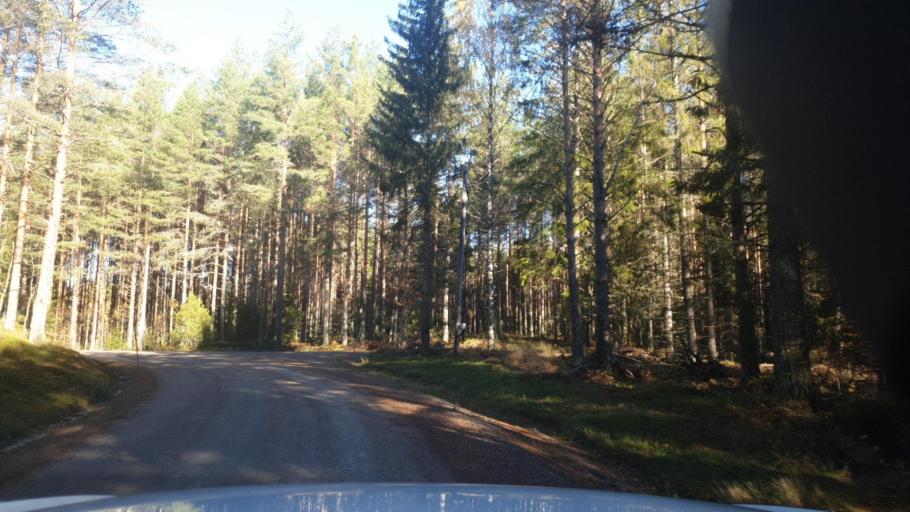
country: SE
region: Vaermland
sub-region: Arvika Kommun
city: Arvika
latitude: 59.5179
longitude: 12.7368
